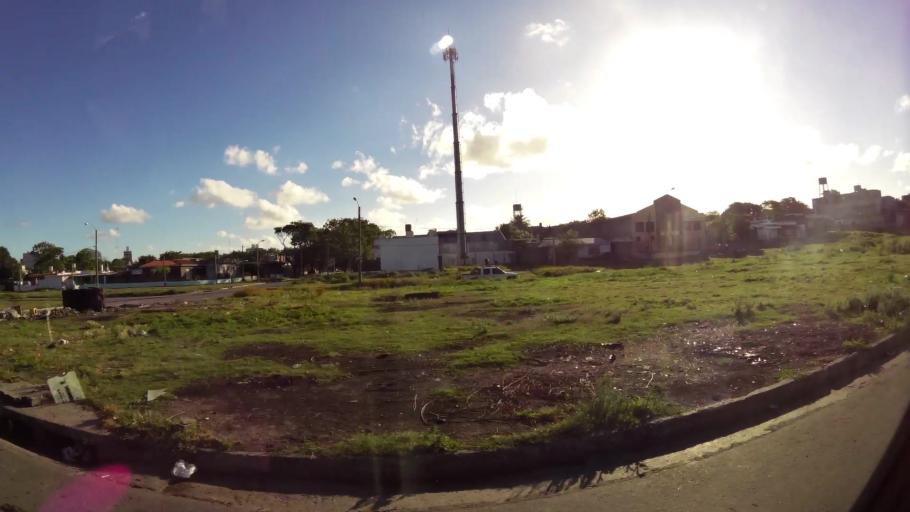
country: UY
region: Montevideo
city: Montevideo
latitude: -34.8809
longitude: -56.1300
